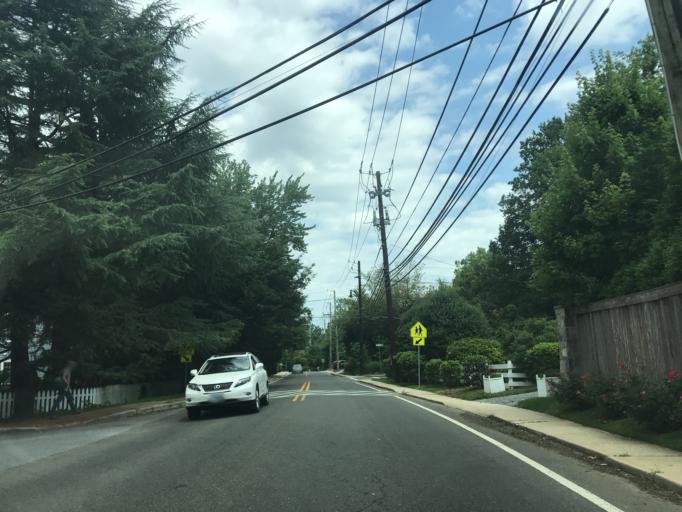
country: US
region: Maryland
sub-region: Montgomery County
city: Chevy Chase
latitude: 38.9774
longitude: -77.0712
